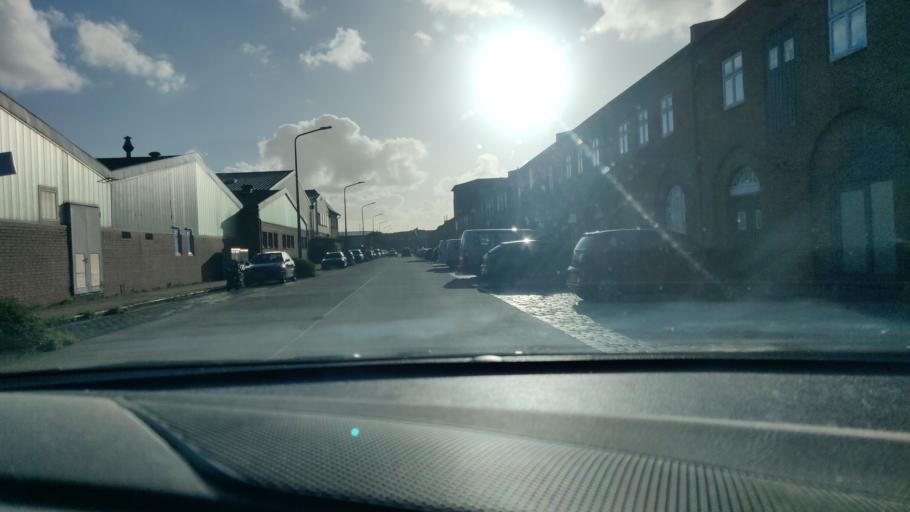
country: DE
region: Lower Saxony
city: Cuxhaven
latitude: 53.8650
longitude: 8.7076
